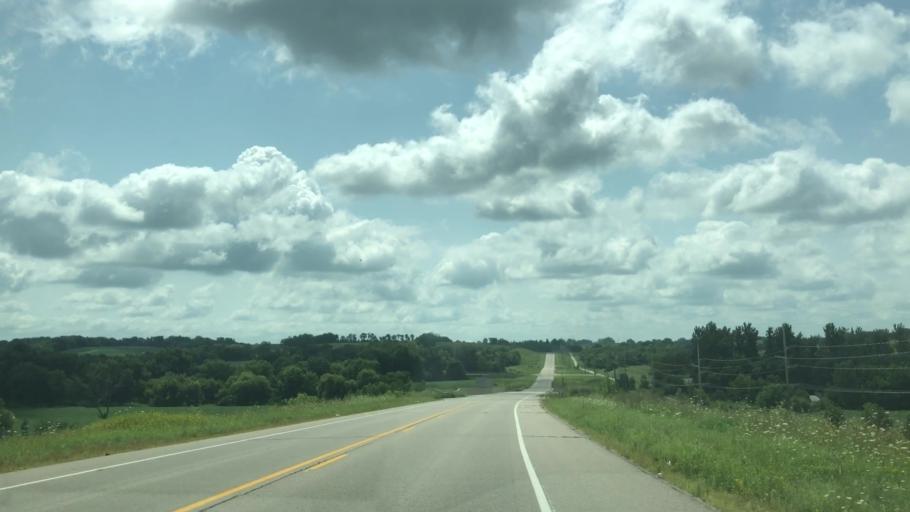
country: US
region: Iowa
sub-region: Marshall County
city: Marshalltown
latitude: 42.0234
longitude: -92.9601
